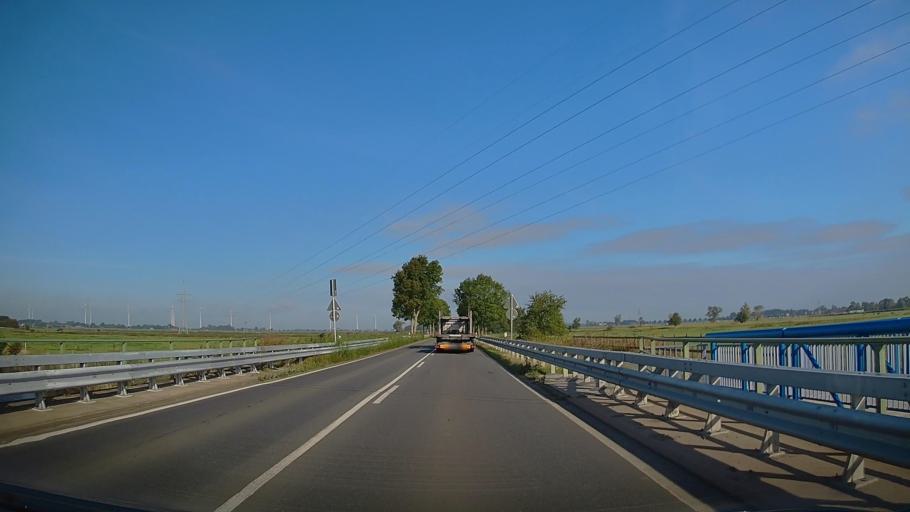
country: DE
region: Lower Saxony
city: Brake (Unterweser)
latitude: 53.3339
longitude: 8.4550
